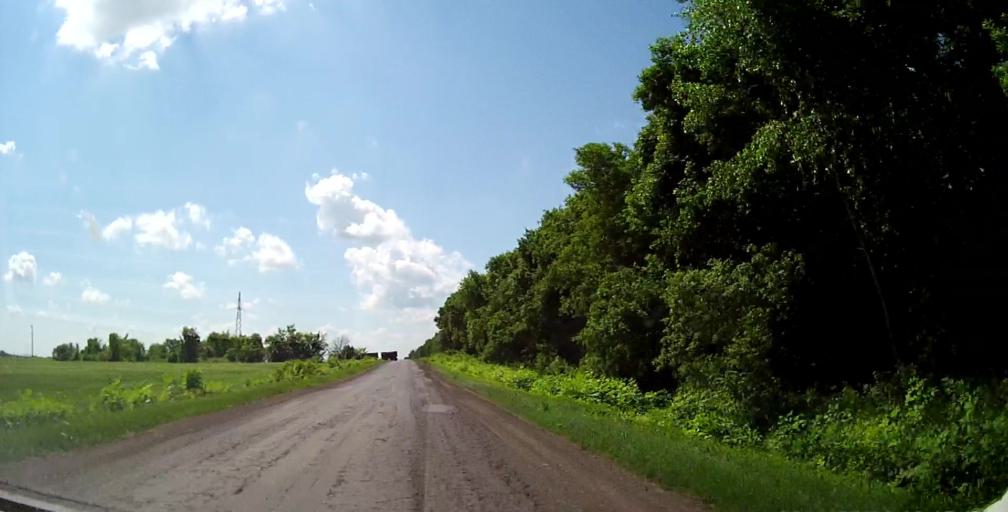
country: RU
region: Lipetsk
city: Chaplygin
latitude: 53.2942
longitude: 39.9561
